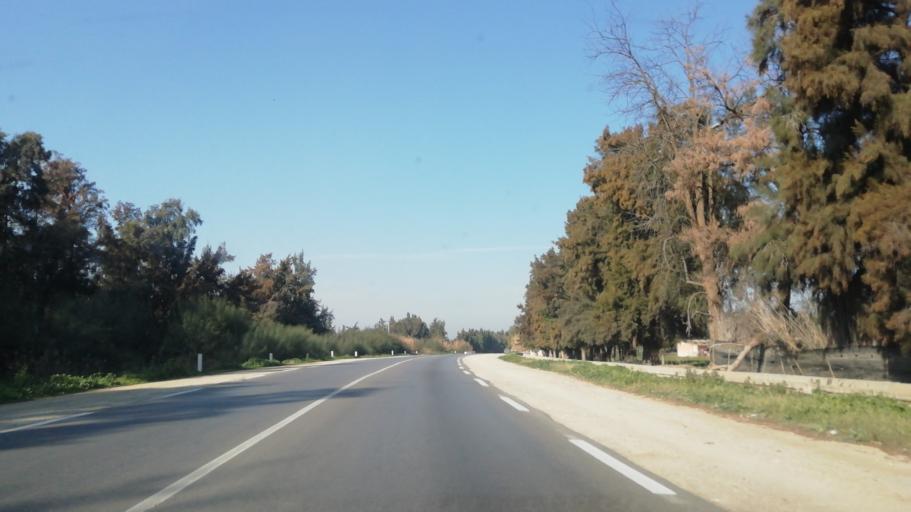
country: DZ
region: Relizane
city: Relizane
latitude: 35.7242
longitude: 0.4827
